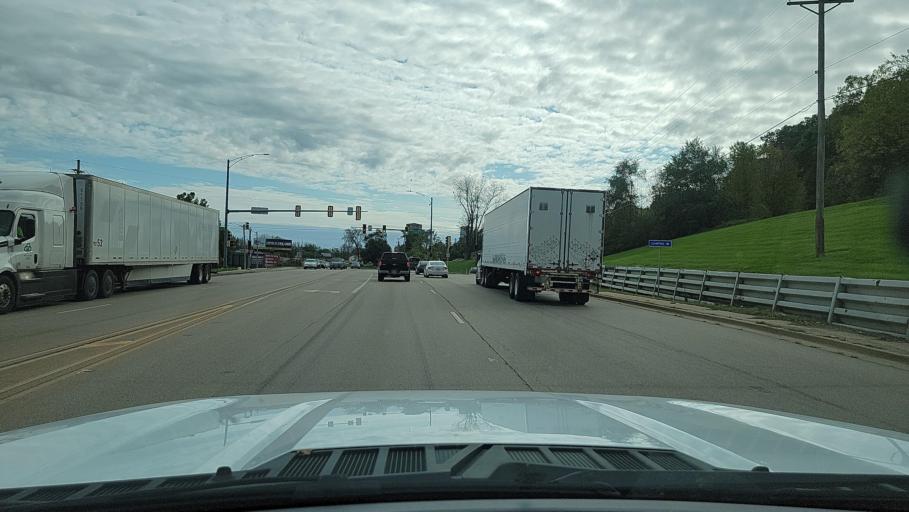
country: US
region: Illinois
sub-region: Peoria County
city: Bartonville
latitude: 40.6400
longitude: -89.6521
